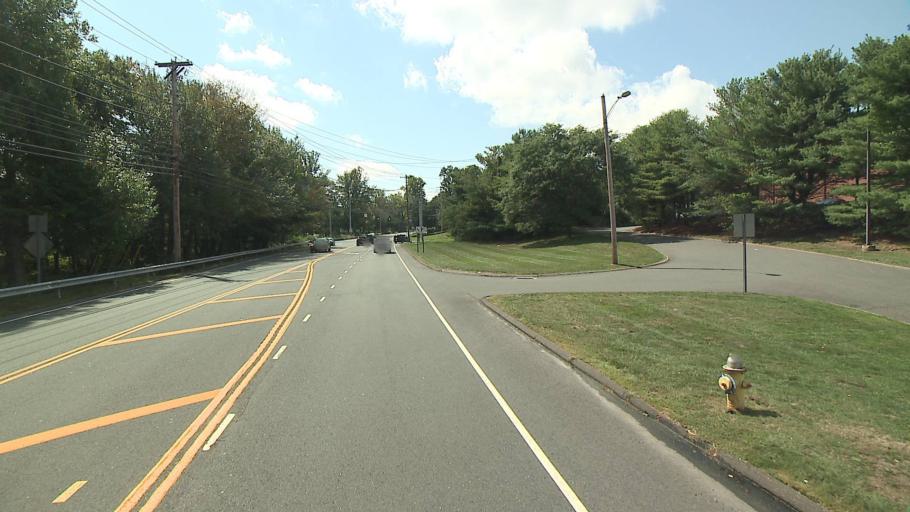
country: US
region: Connecticut
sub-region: Fairfield County
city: Shelton
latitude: 41.2645
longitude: -73.1335
